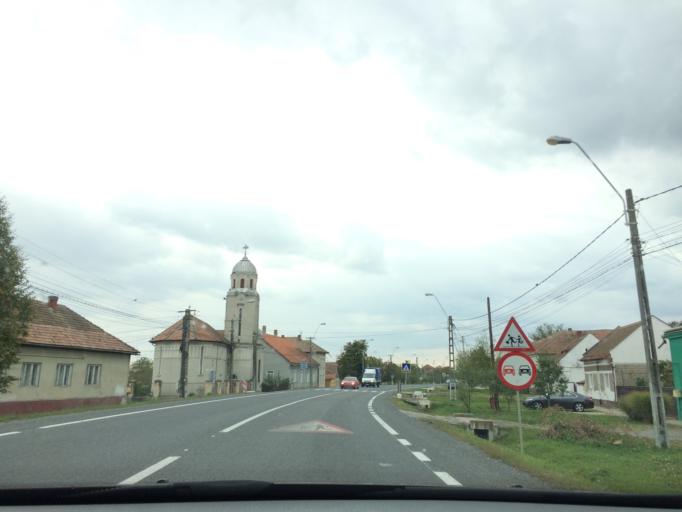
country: RO
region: Timis
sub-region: Oras Recas
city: Izvin
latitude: 45.7993
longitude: 21.4611
